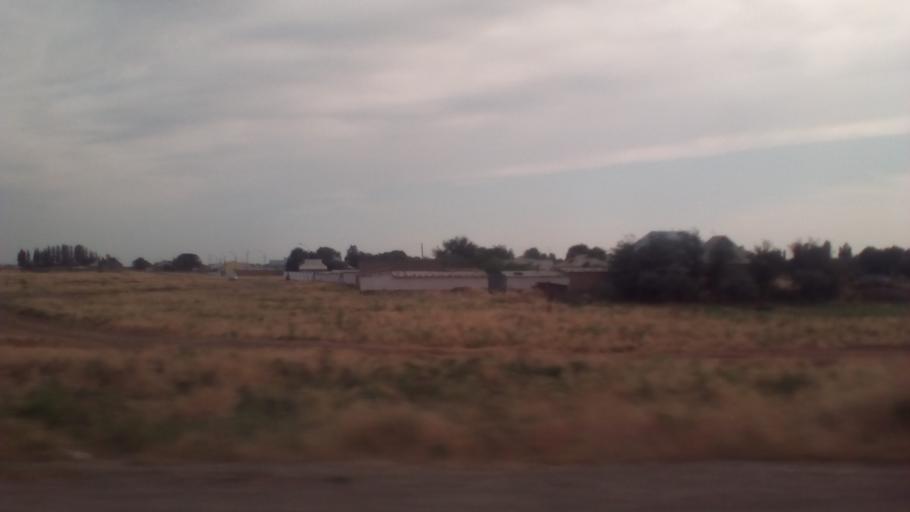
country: KZ
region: Ongtustik Qazaqstan
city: Temirlanovka
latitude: 42.7937
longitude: 69.2033
